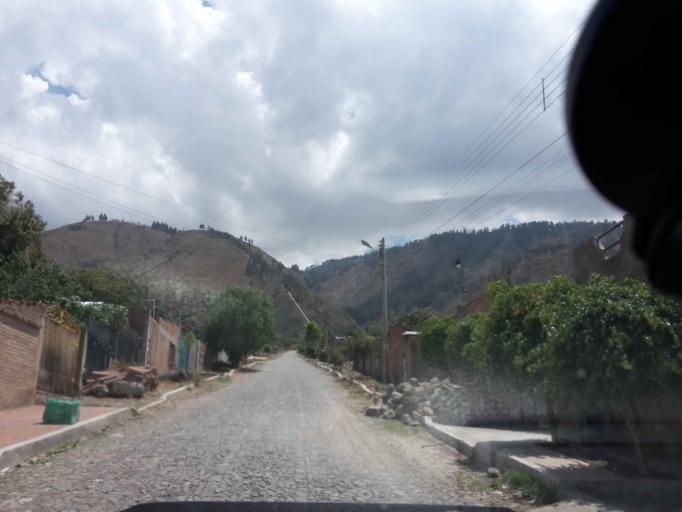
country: BO
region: Cochabamba
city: Cochabamba
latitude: -17.3230
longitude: -66.2226
